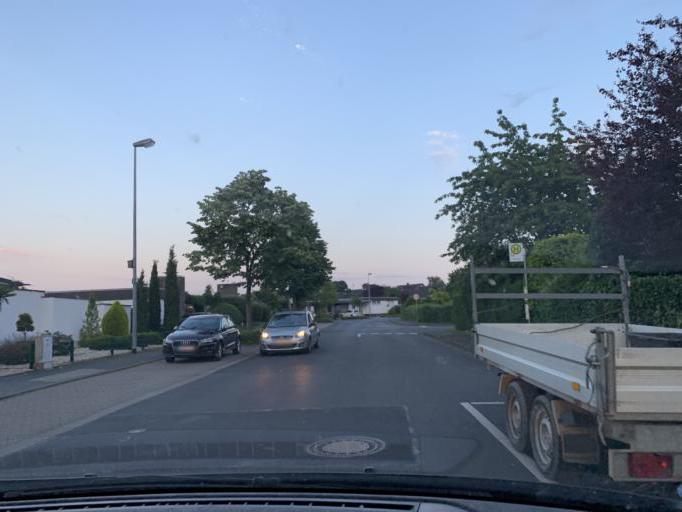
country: DE
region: North Rhine-Westphalia
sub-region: Regierungsbezirk Koln
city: Pulheim
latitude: 50.9985
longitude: 6.8179
